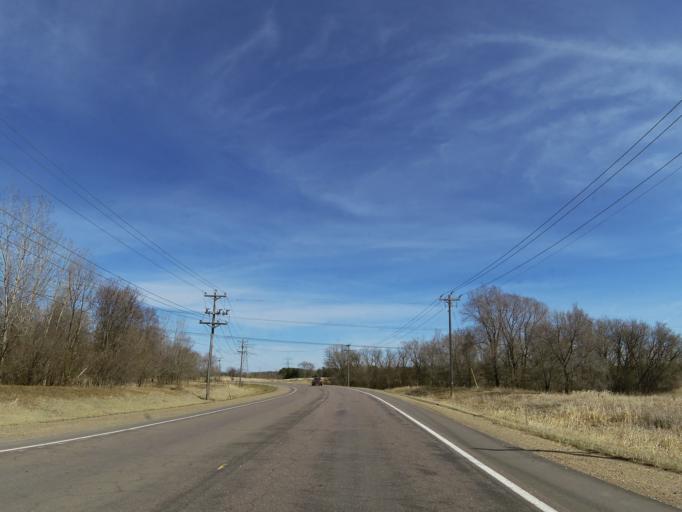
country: US
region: Minnesota
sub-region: Washington County
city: Lake Elmo
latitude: 44.9455
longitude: -92.8553
